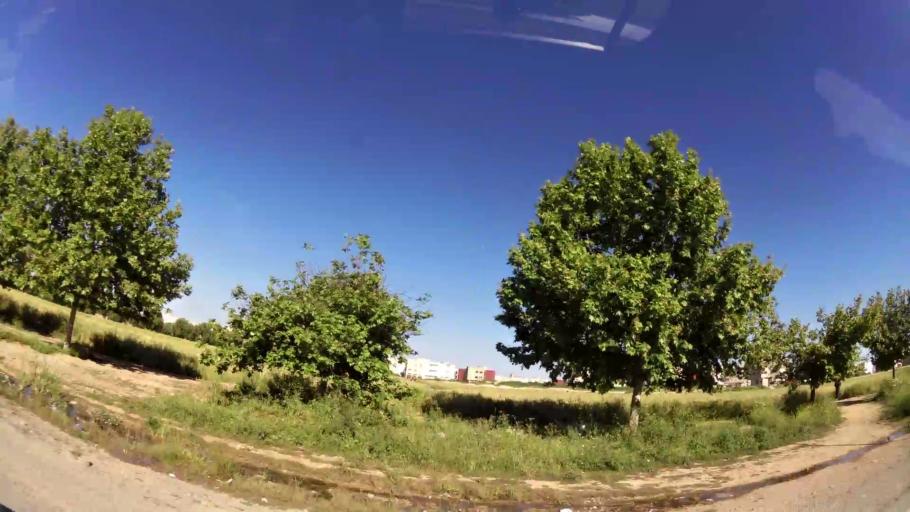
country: MA
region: Fes-Boulemane
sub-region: Fes
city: Fes
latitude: 34.0085
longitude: -5.0213
